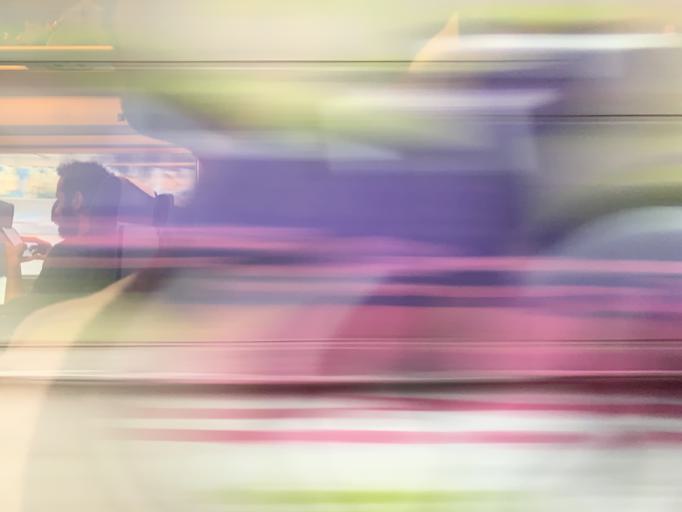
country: ES
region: Catalonia
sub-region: Provincia de Barcelona
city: L'Hospitalet de Llobregat
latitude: 41.3466
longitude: 2.1149
